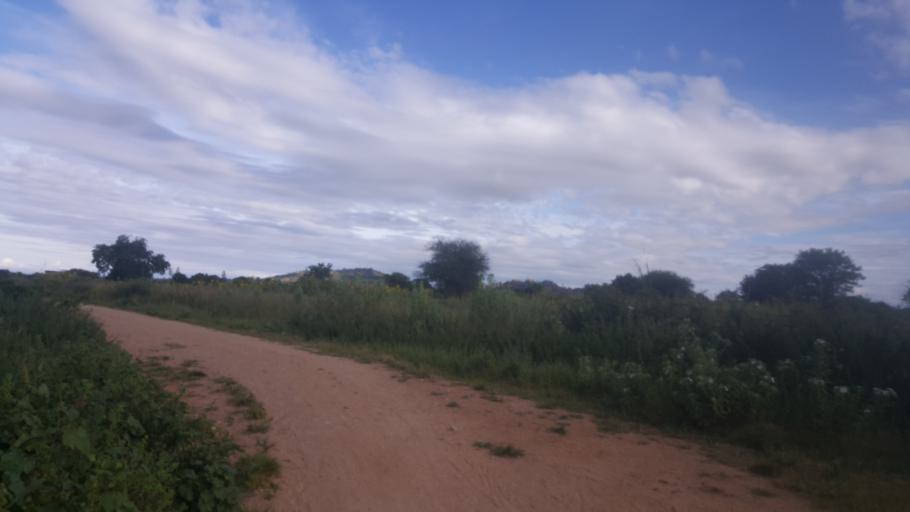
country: TZ
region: Dodoma
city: Dodoma
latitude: -6.0901
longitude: 35.5289
